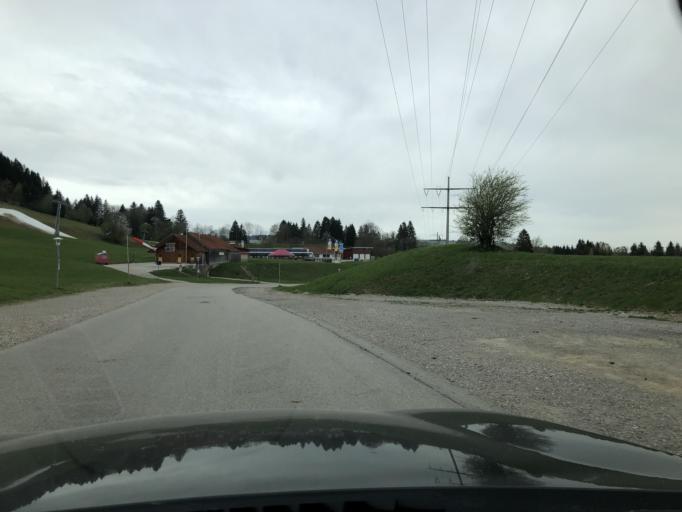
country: DE
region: Bavaria
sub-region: Swabia
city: Nesselwang
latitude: 47.6177
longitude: 10.5002
